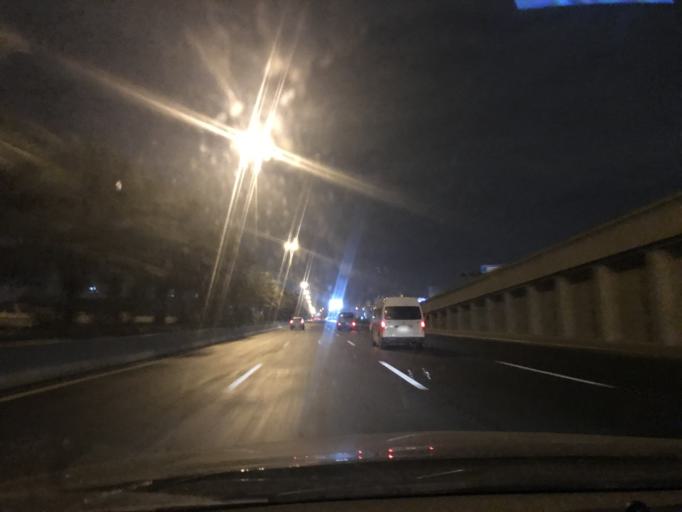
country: SA
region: Ar Riyad
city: Riyadh
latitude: 24.7486
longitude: 46.6181
